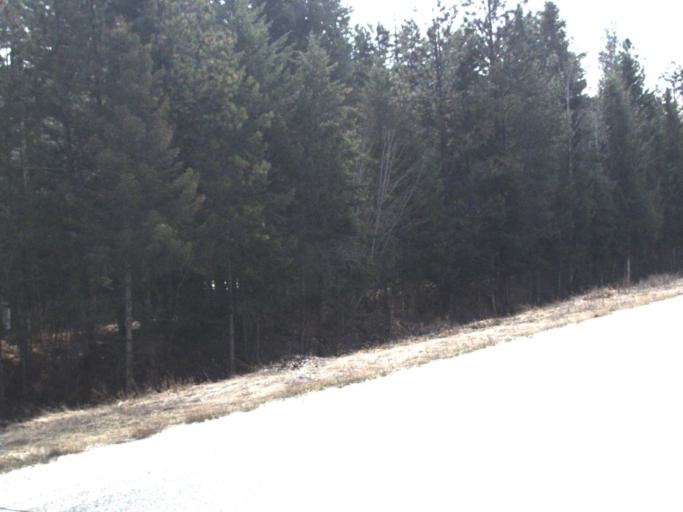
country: US
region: Washington
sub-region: Pend Oreille County
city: Newport
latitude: 48.4893
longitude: -117.2690
